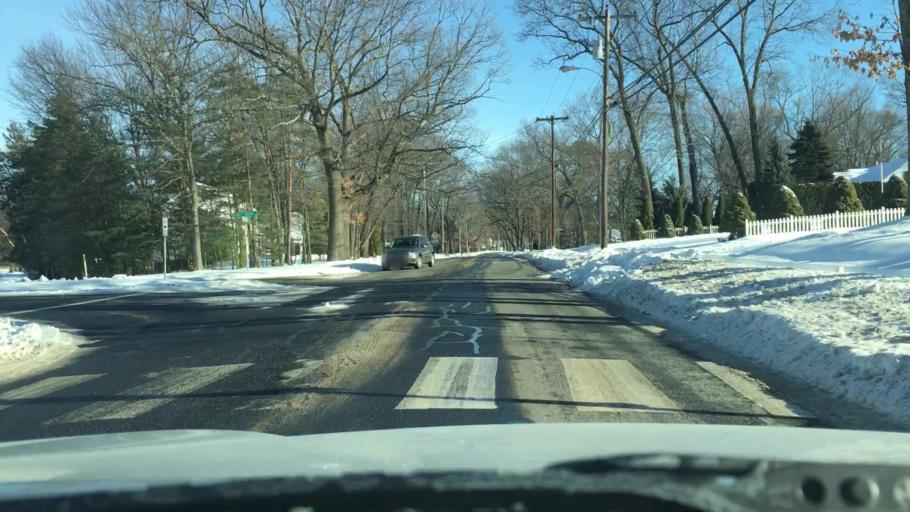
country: US
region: Connecticut
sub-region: Hartford County
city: Sherwood Manor
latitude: 42.0372
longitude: -72.5623
